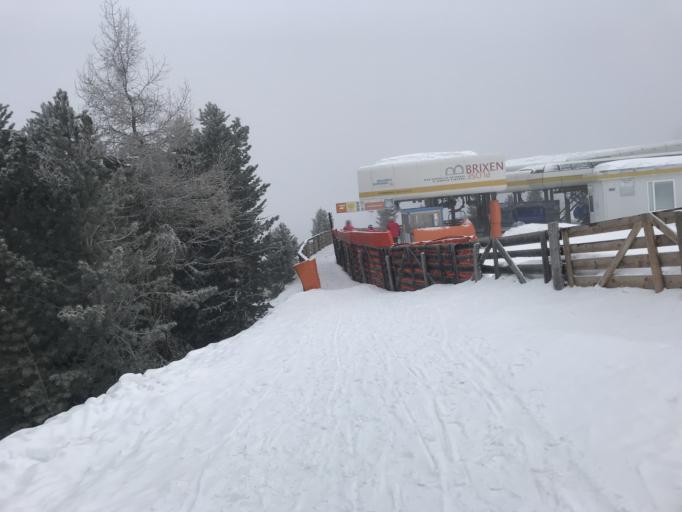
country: IT
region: Trentino-Alto Adige
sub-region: Bolzano
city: San Pietro
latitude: 46.6836
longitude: 11.7096
